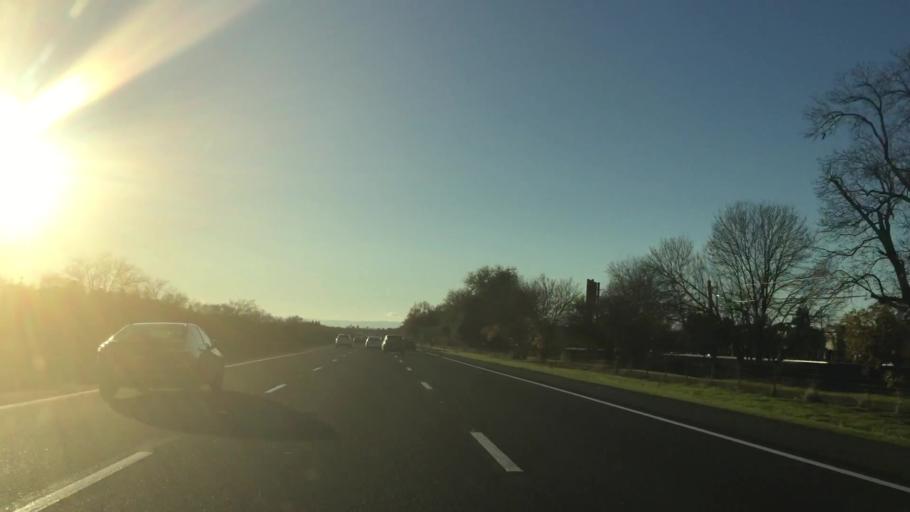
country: US
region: California
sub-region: Yolo County
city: Davis
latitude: 38.5489
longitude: -121.7141
